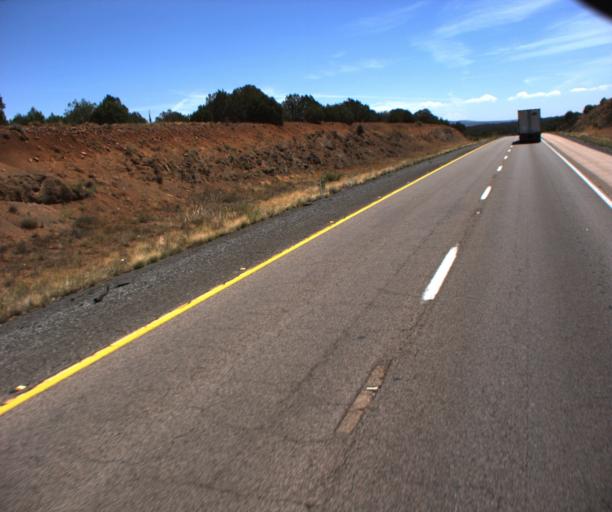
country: US
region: Arizona
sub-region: Mohave County
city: Peach Springs
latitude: 35.2073
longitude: -113.2803
